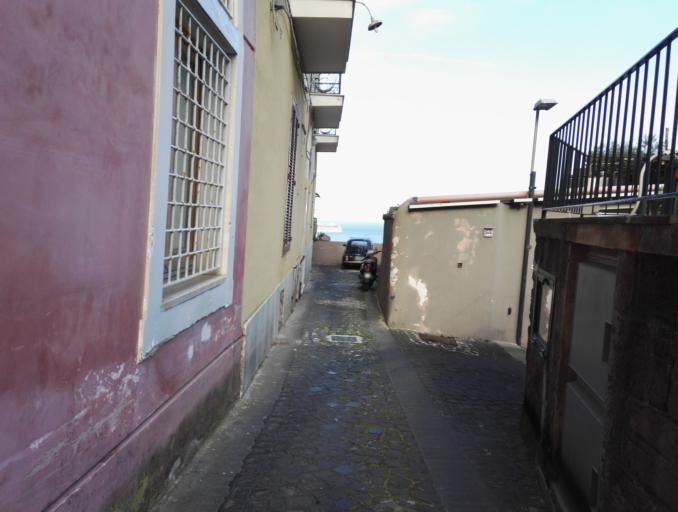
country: IT
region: Campania
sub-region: Provincia di Napoli
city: Meta
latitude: 40.6450
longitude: 14.4079
